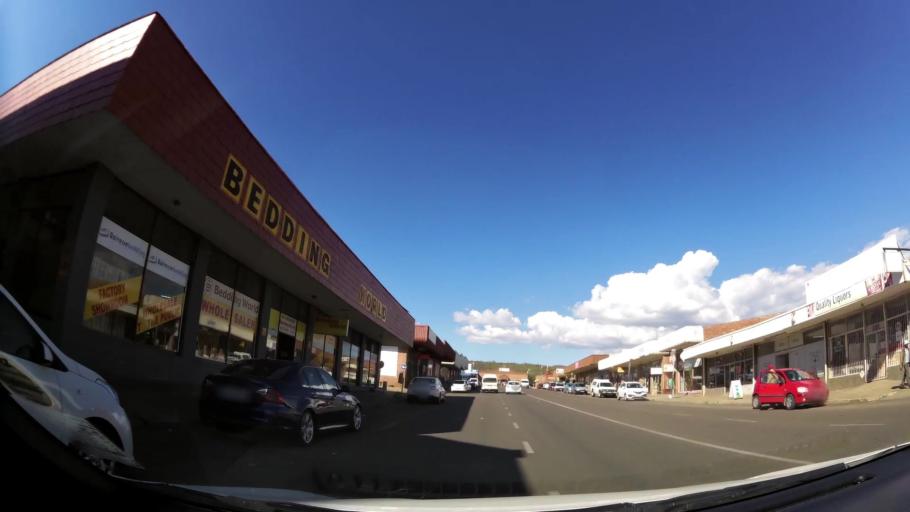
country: ZA
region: Limpopo
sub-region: Waterberg District Municipality
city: Mokopane
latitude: -24.1817
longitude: 29.0166
